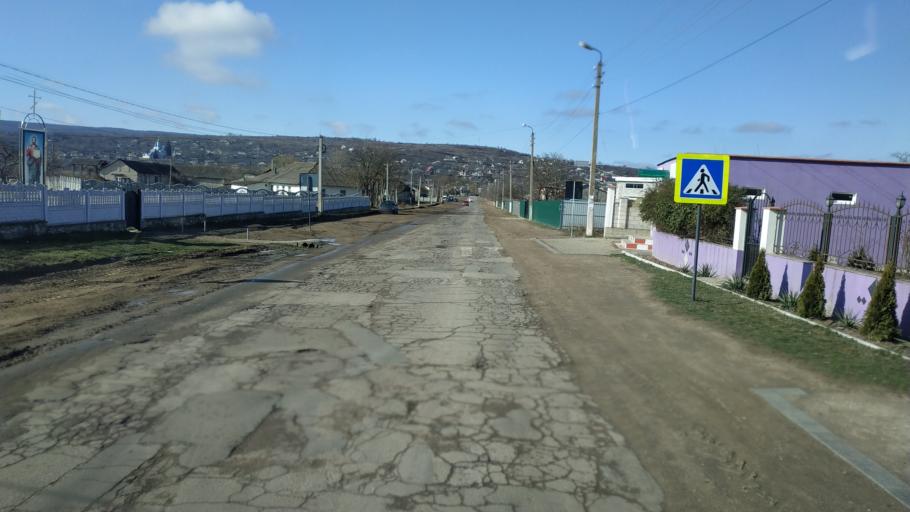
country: MD
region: Hincesti
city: Hincesti
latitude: 46.9319
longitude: 28.6599
